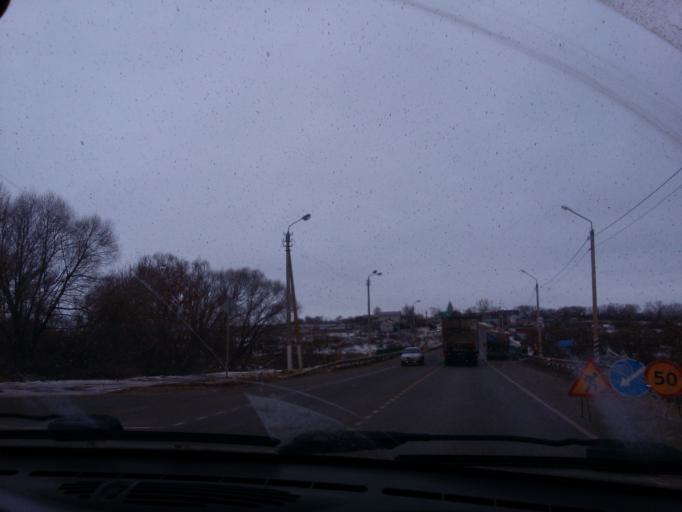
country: RU
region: Tula
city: Shchekino
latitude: 53.9031
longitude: 37.4633
